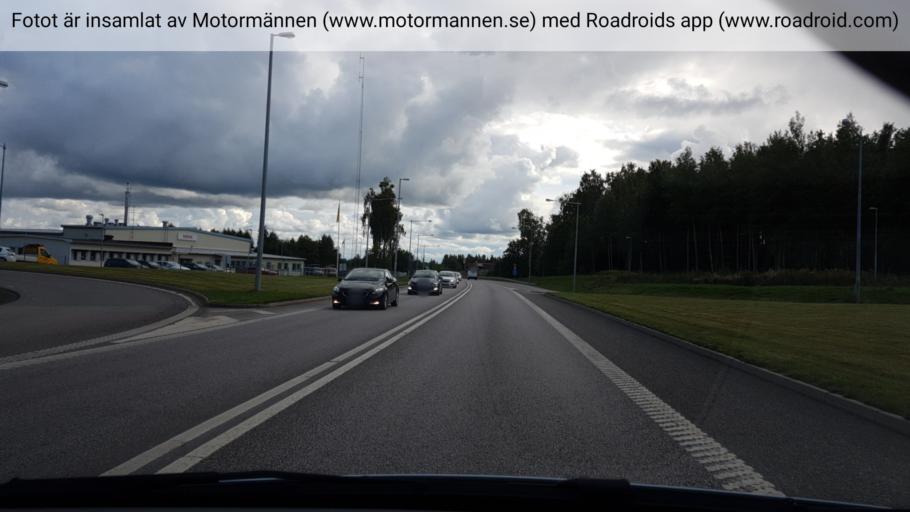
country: SE
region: Vaestra Goetaland
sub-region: Skovde Kommun
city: Skoevde
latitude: 58.4013
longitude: 13.8717
